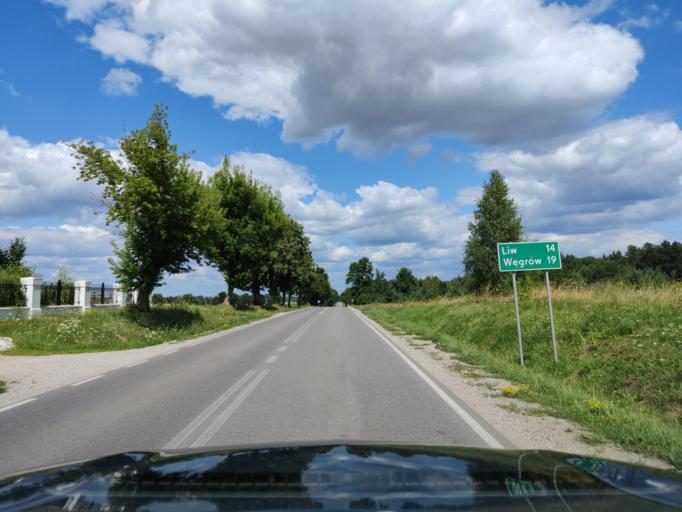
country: PL
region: Masovian Voivodeship
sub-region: Powiat wegrowski
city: Grebkow
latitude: 52.2548
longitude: 21.8961
